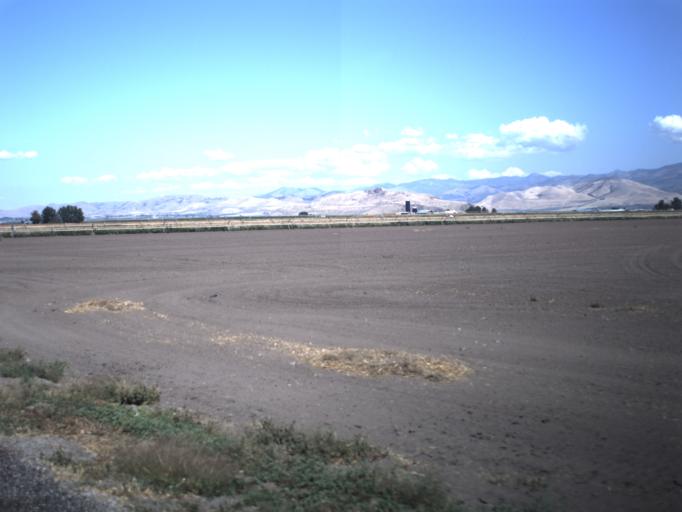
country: US
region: Utah
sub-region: Cache County
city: Lewiston
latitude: 41.9802
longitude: -111.8762
